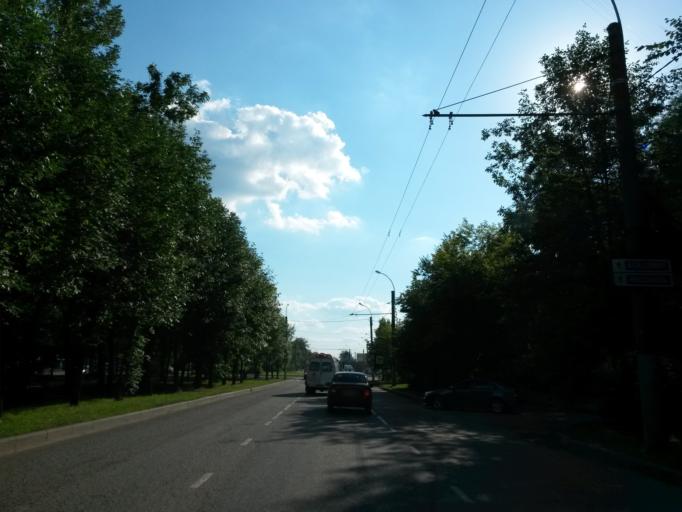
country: RU
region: Ivanovo
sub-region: Gorod Ivanovo
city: Ivanovo
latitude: 56.9610
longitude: 41.0106
